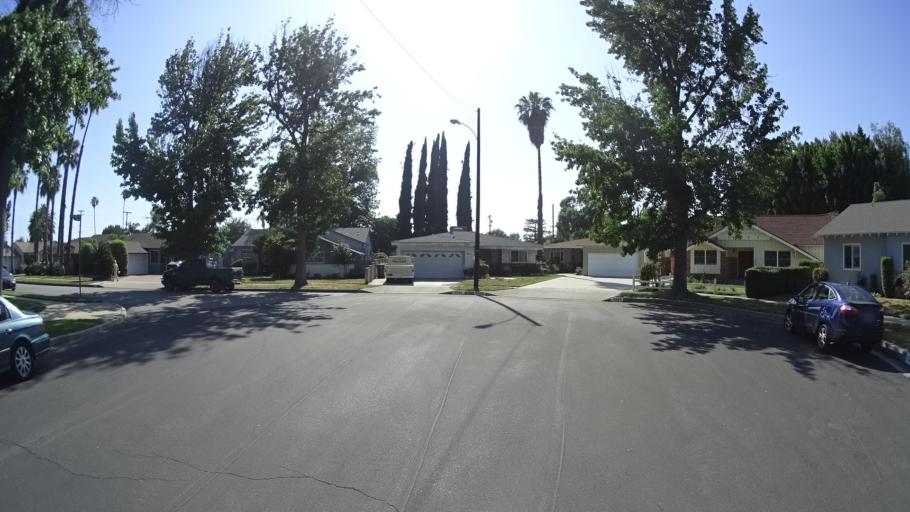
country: US
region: California
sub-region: Los Angeles County
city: Van Nuys
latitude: 34.1895
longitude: -118.4288
